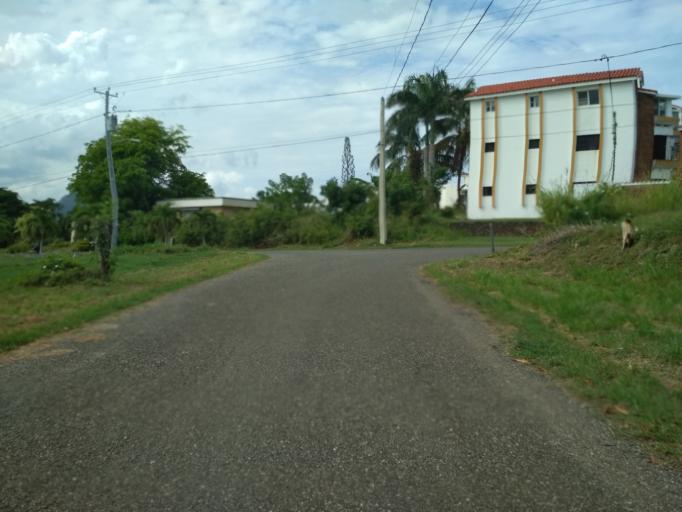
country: DO
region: Puerto Plata
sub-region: Puerto Plata
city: Puerto Plata
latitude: 19.8118
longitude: -70.7125
